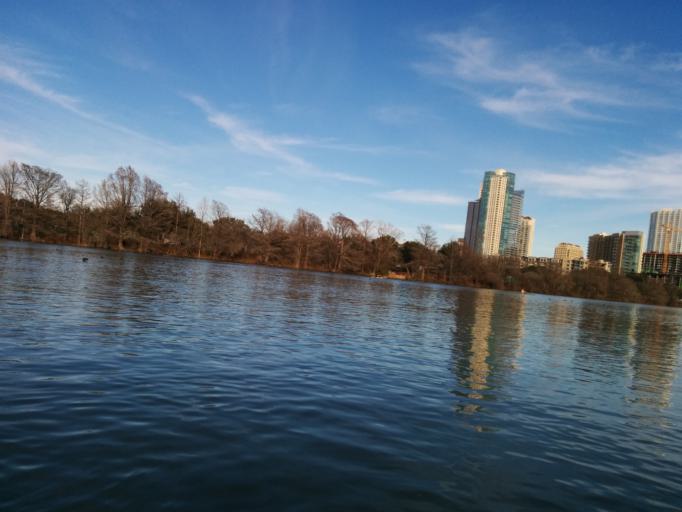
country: US
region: Texas
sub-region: Travis County
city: Austin
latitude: 30.2671
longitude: -97.7614
